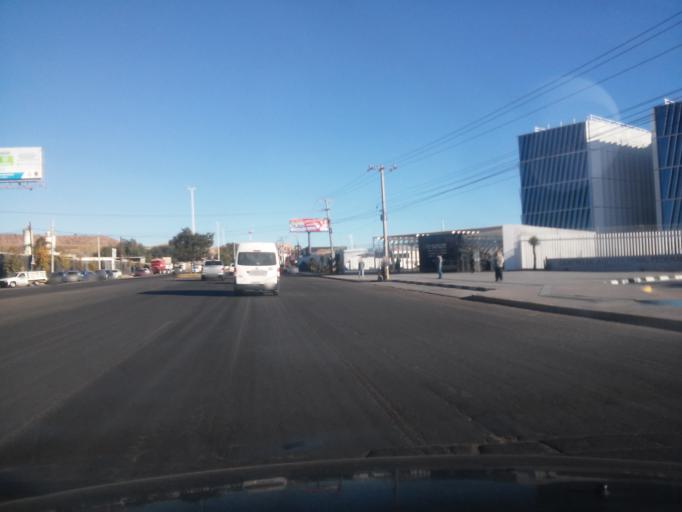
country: MX
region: Durango
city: Victoria de Durango
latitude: 24.0433
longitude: -104.6581
